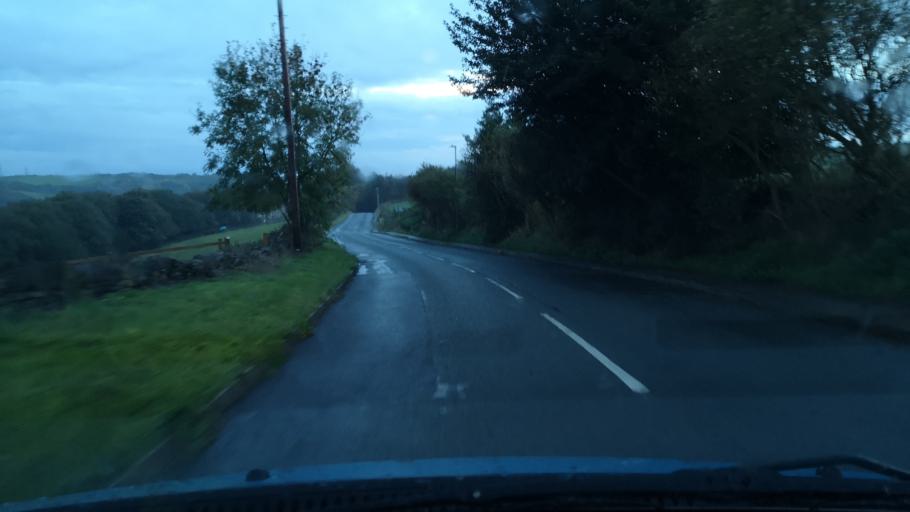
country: GB
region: England
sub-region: Kirklees
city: Batley
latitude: 53.7300
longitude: -1.6392
